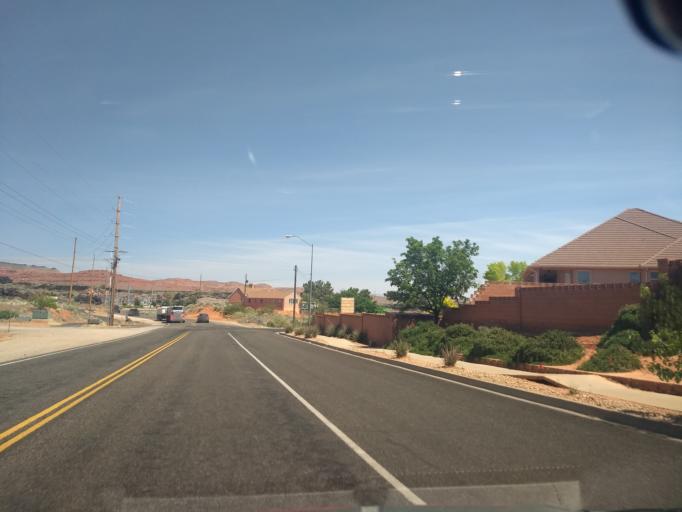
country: US
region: Utah
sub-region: Washington County
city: Santa Clara
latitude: 37.1465
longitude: -113.6571
